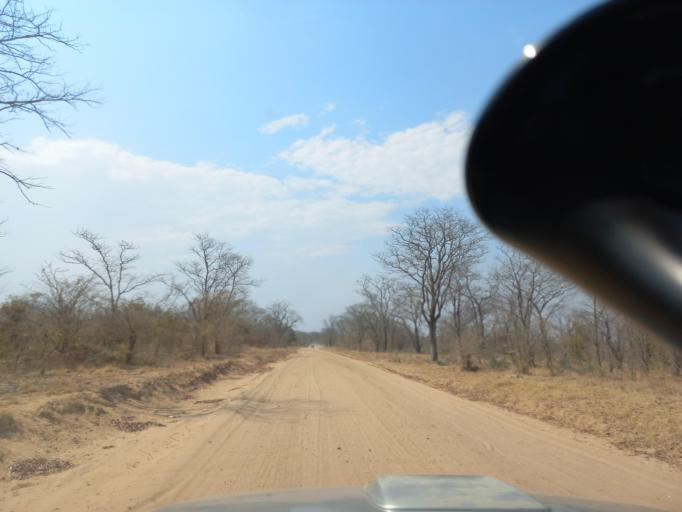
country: ZW
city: Chirundu
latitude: -15.9344
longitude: 28.9150
